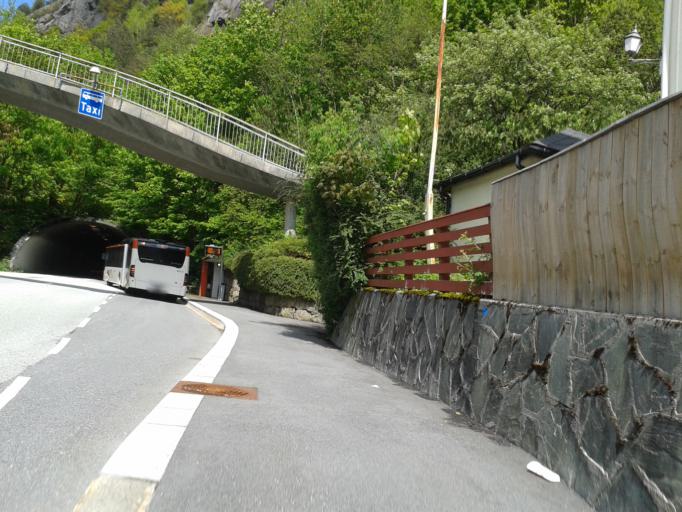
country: NO
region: Hordaland
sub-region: Bergen
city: Bergen
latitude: 60.4141
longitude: 5.3220
